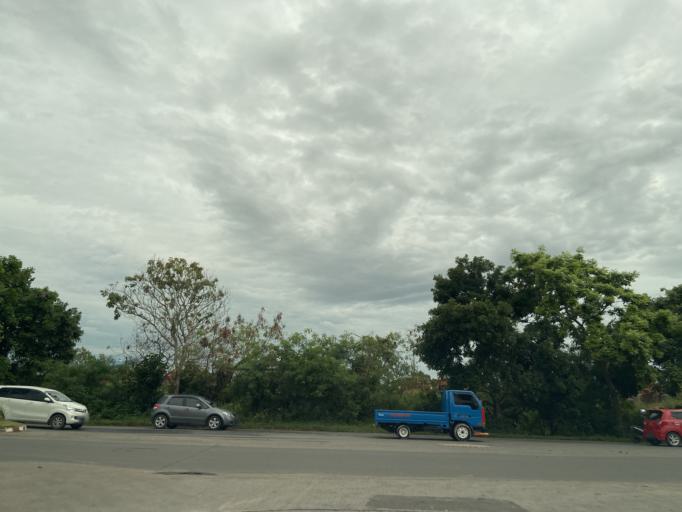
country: SG
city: Singapore
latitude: 1.1141
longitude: 104.0634
